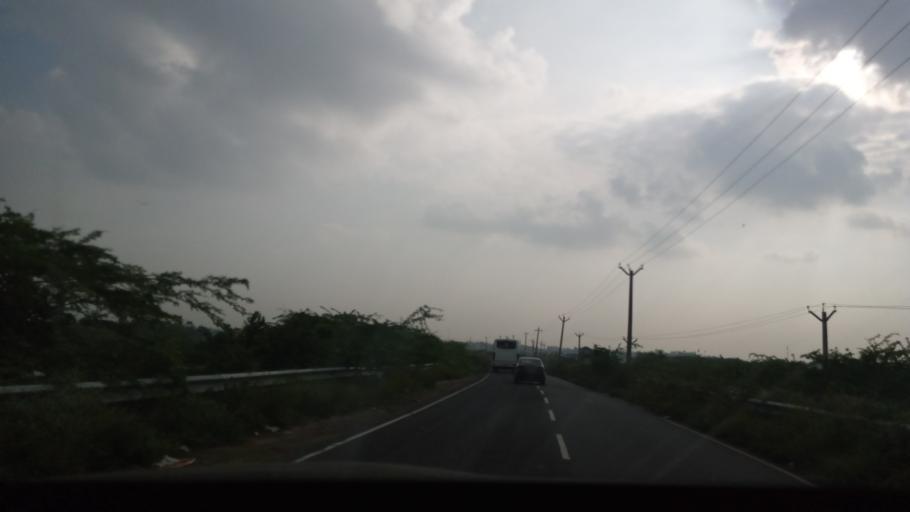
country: IN
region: Tamil Nadu
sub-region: Kancheepuram
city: Injambakkam
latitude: 12.7838
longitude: 80.2371
